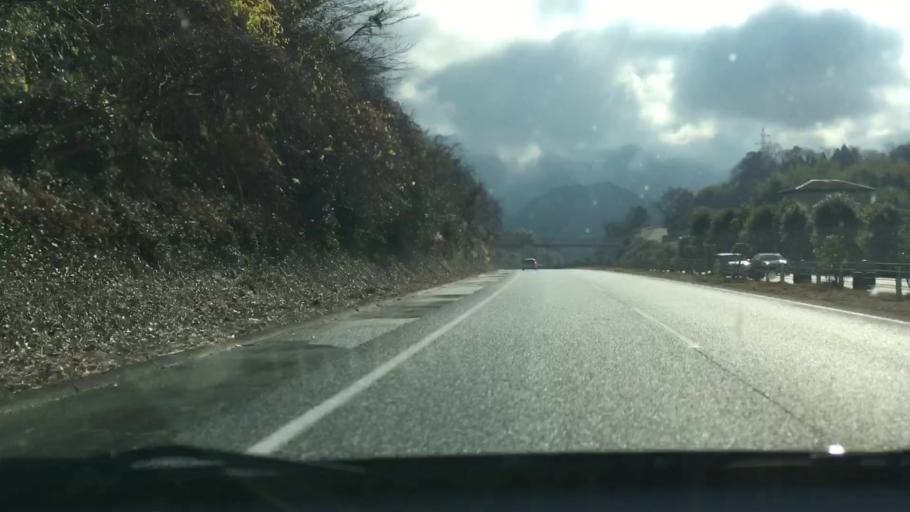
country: JP
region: Kumamoto
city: Matsubase
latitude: 32.5572
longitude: 130.6955
